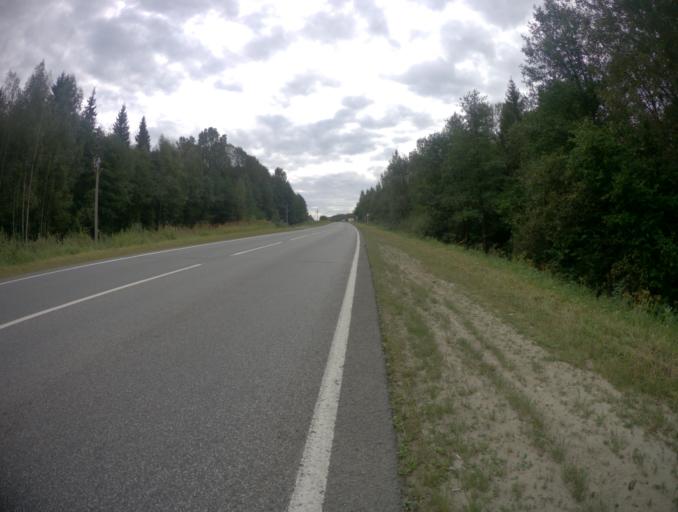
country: RU
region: Vladimir
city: Golovino
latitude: 55.9709
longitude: 40.5485
